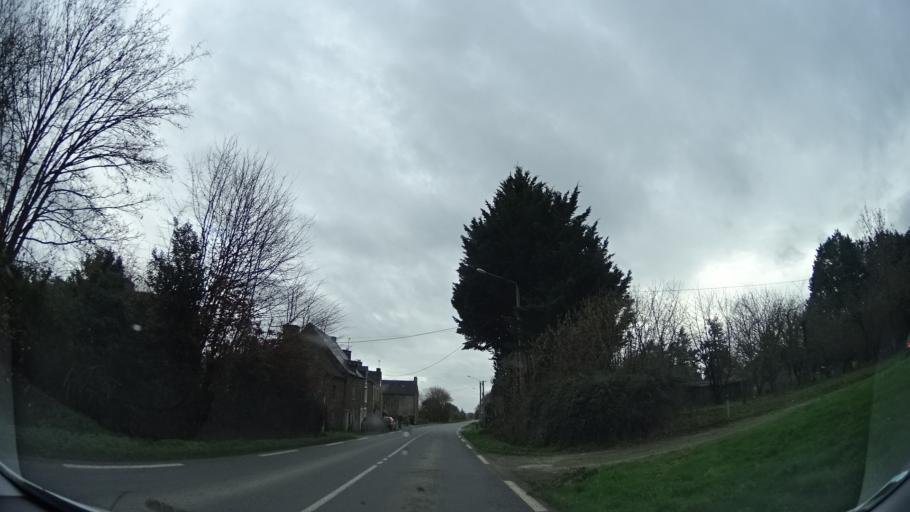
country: FR
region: Brittany
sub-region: Departement des Cotes-d'Armor
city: Evran
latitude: 48.3969
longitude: -1.9798
